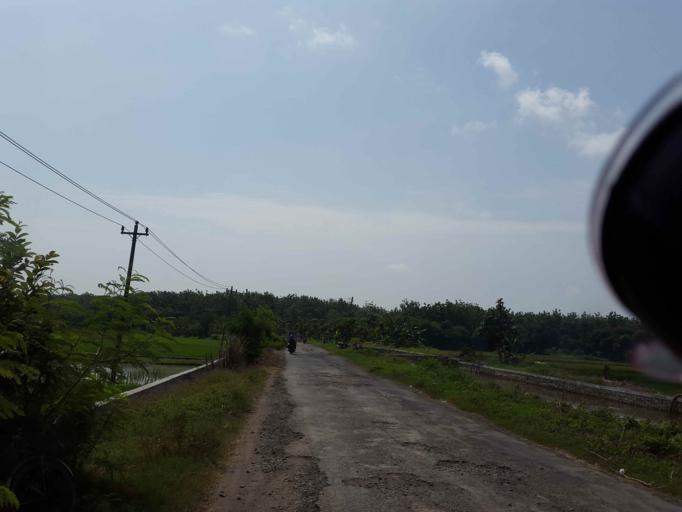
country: ID
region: Central Java
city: Pemalang
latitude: -6.9513
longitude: 109.3591
